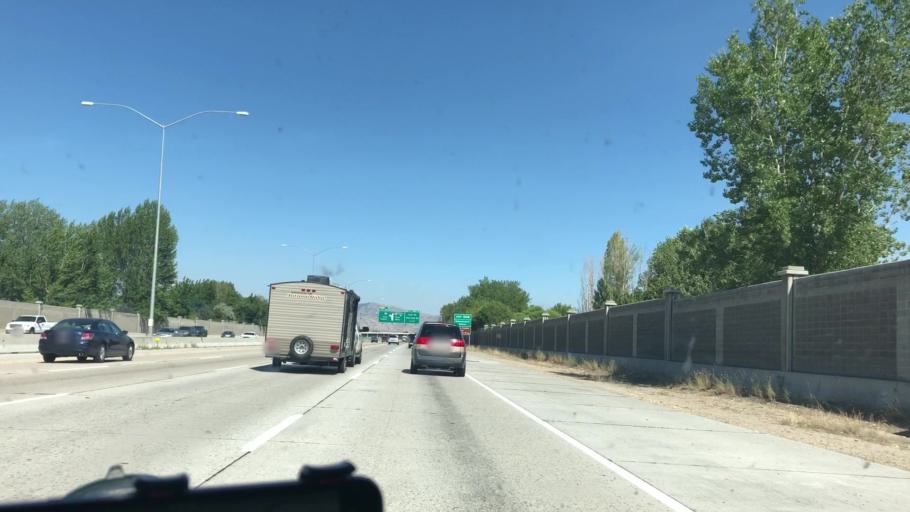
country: US
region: Idaho
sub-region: Ada County
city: Garden City
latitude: 43.5971
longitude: -116.3062
